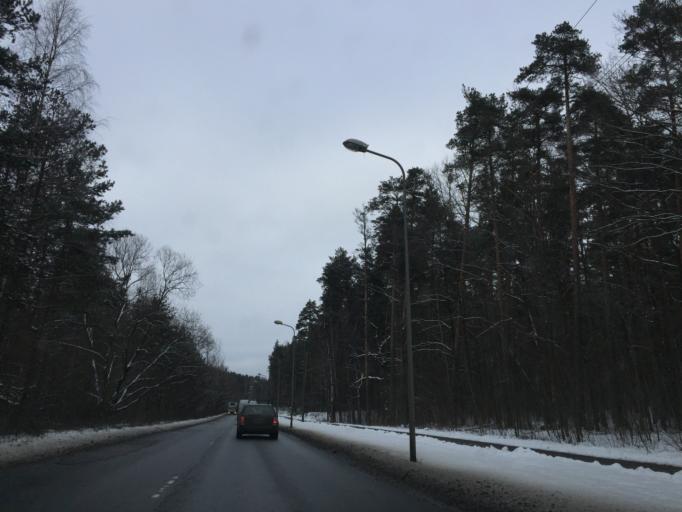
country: LV
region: Stopini
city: Ulbroka
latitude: 56.9646
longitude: 24.2525
